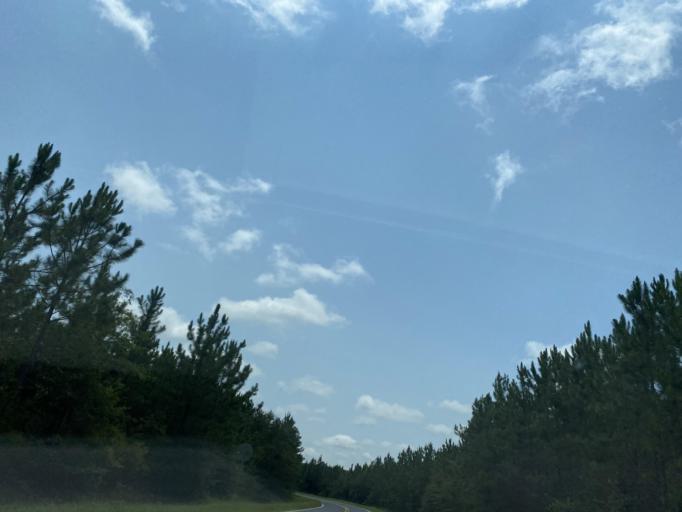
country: US
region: Georgia
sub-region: Telfair County
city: Lumber City
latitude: 31.9695
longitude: -82.7058
